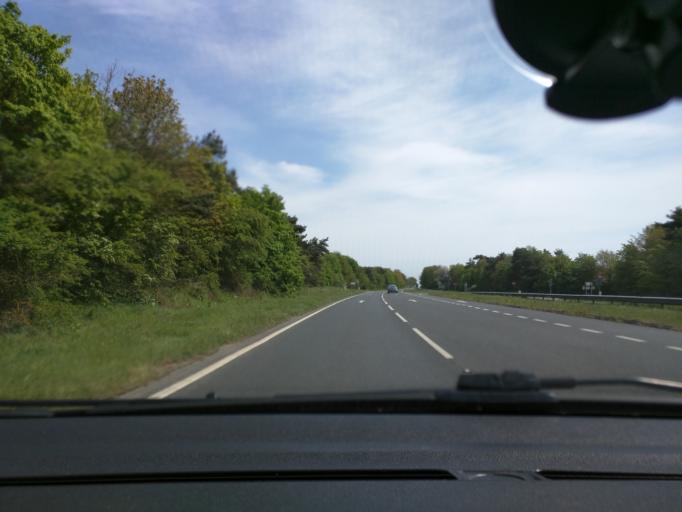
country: GB
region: England
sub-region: Suffolk
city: Wrentham
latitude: 52.3568
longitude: 1.6199
